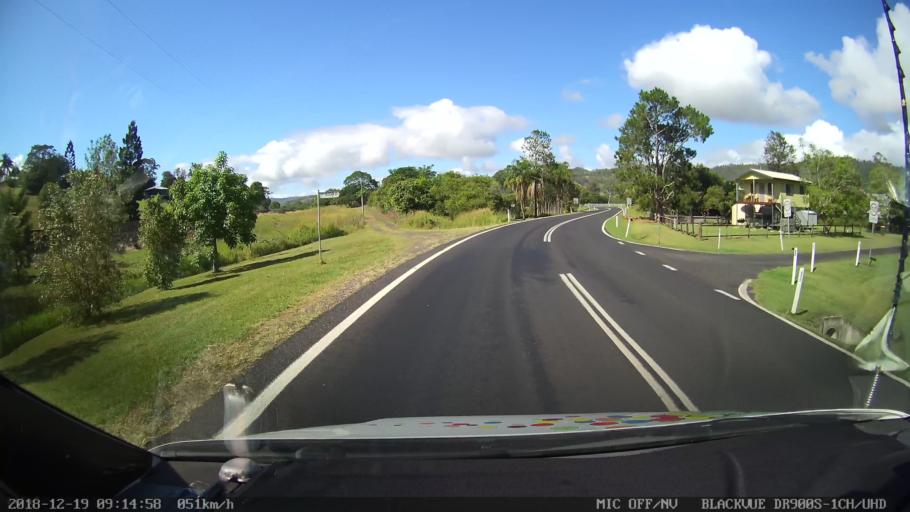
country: AU
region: New South Wales
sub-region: Kyogle
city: Kyogle
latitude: -28.5103
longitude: 152.9642
